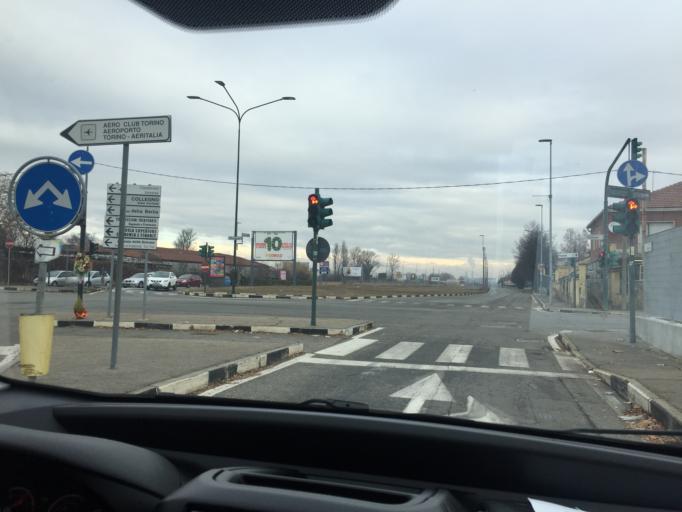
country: IT
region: Piedmont
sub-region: Provincia di Torino
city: Lesna
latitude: 45.0820
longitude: 7.6147
